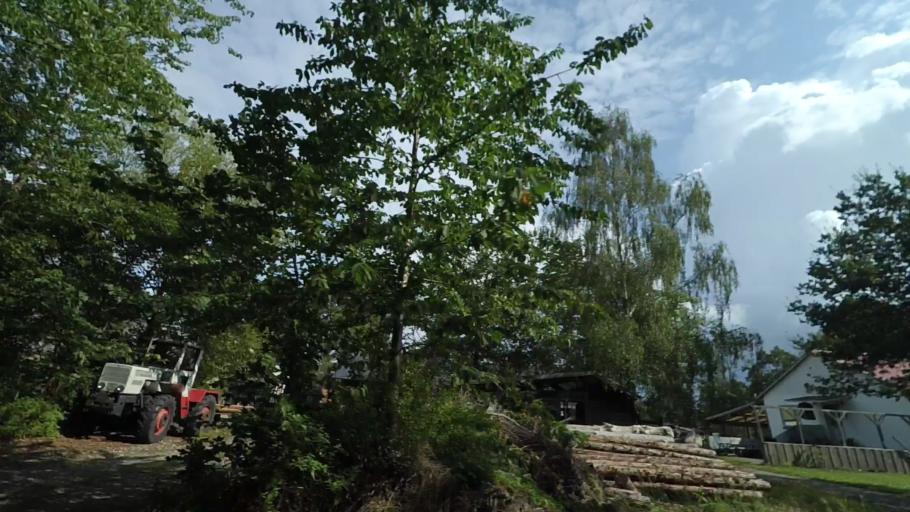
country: DK
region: Central Jutland
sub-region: Syddjurs Kommune
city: Ryomgard
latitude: 56.4621
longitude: 10.5273
